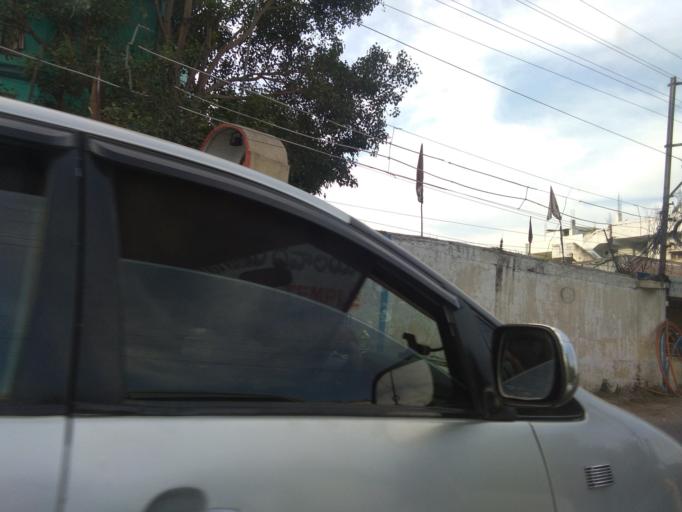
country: IN
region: Telangana
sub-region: Rangareddi
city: Quthbullapur
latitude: 17.4626
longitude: 78.4718
